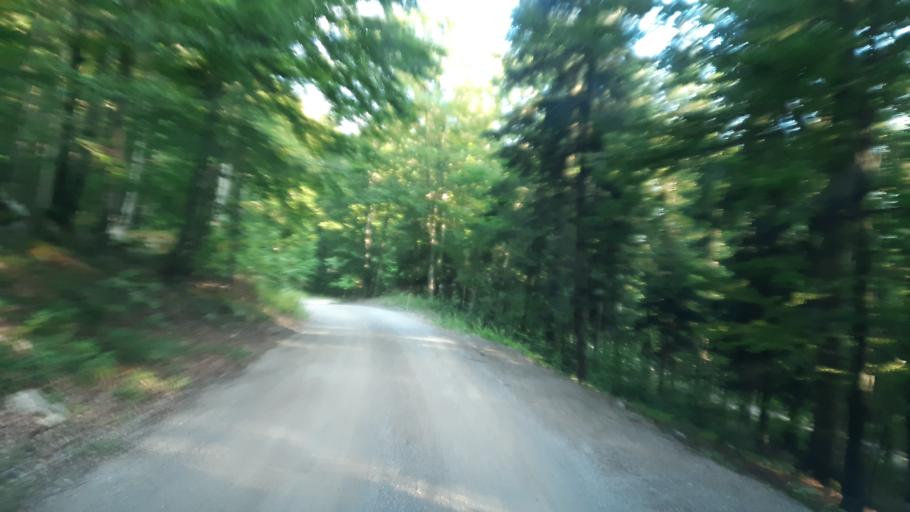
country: SI
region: Kocevje
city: Kocevje
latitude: 45.6720
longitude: 14.9747
